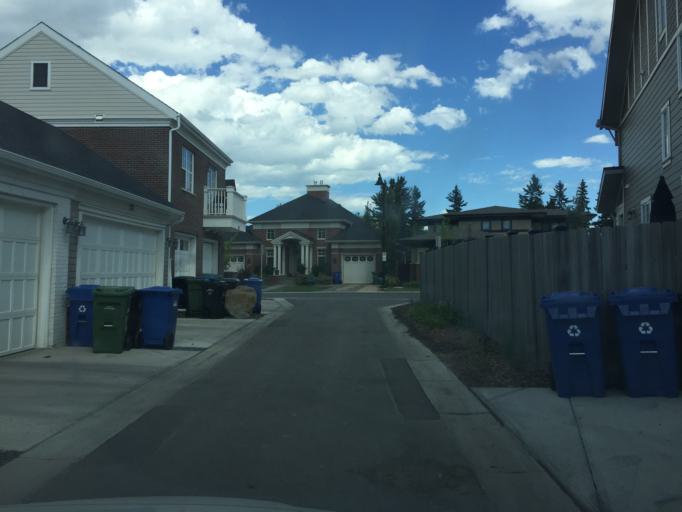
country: CA
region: Alberta
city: Calgary
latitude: 51.0181
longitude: -114.1302
